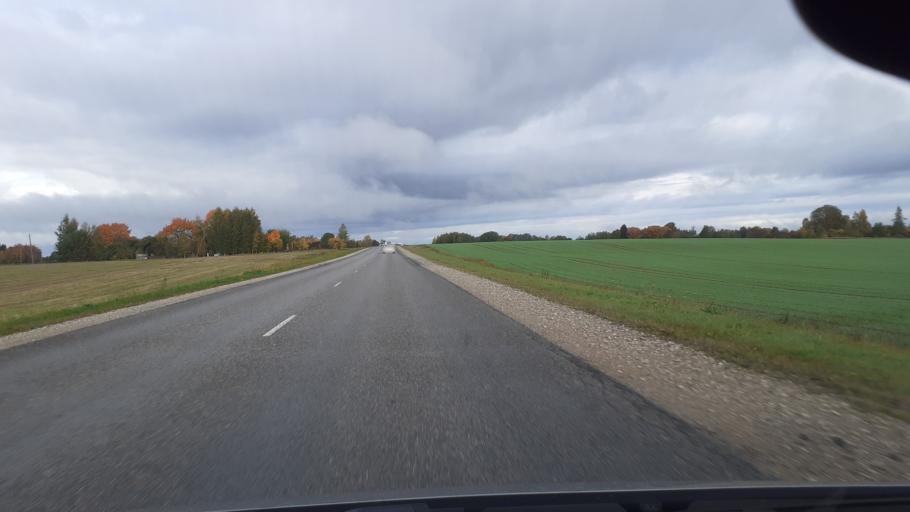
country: LV
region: Kuldigas Rajons
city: Kuldiga
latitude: 56.9925
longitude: 21.9109
